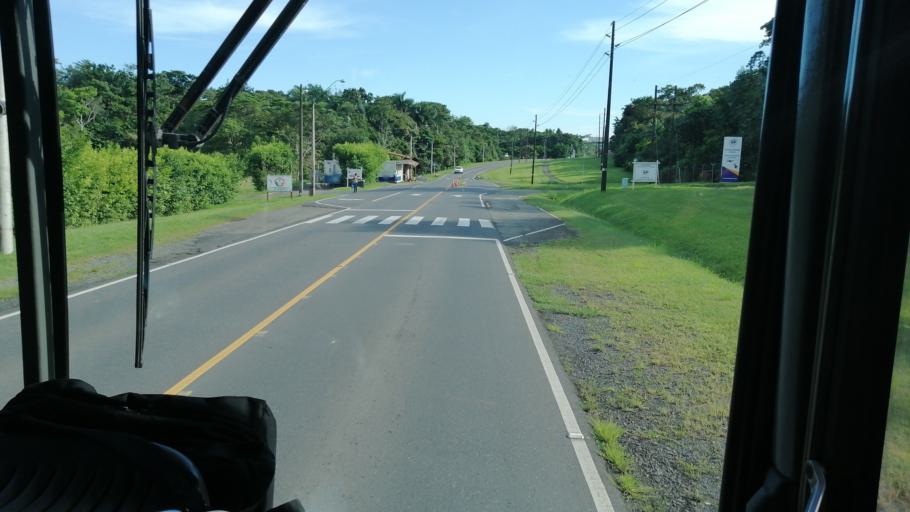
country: PA
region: Panama
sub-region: Distrito de Panama
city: Ancon
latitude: 8.9353
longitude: -79.5910
